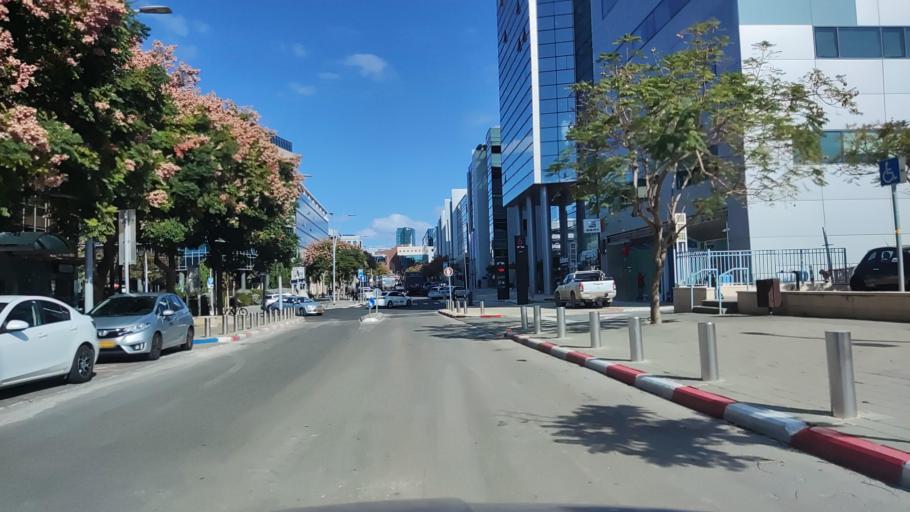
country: IL
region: Tel Aviv
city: Herzliya Pituah
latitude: 32.1577
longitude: 34.8080
